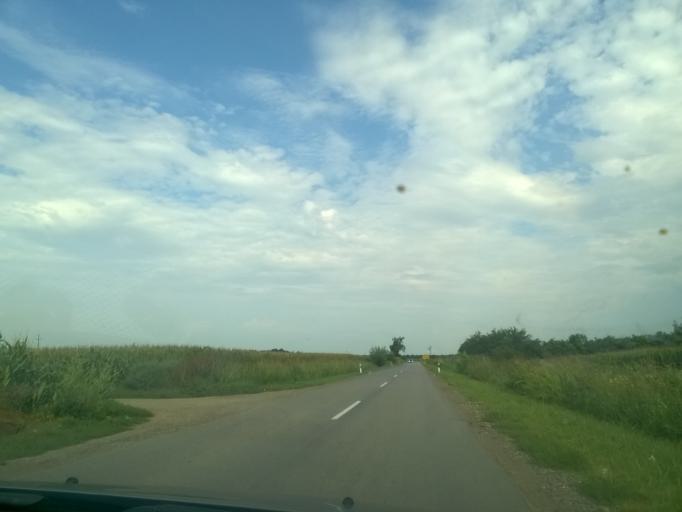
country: RS
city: Ecka
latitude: 45.3193
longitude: 20.4619
